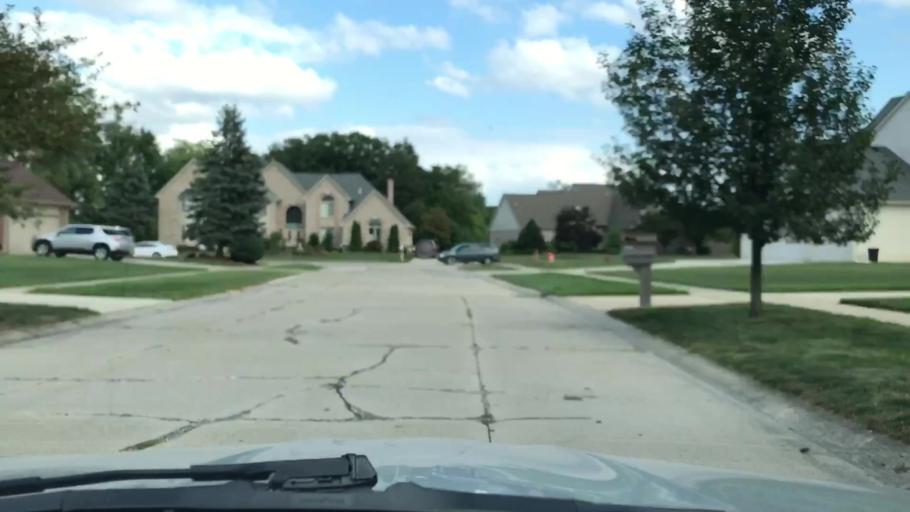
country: US
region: Michigan
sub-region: Macomb County
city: Utica
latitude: 42.6052
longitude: -83.0836
